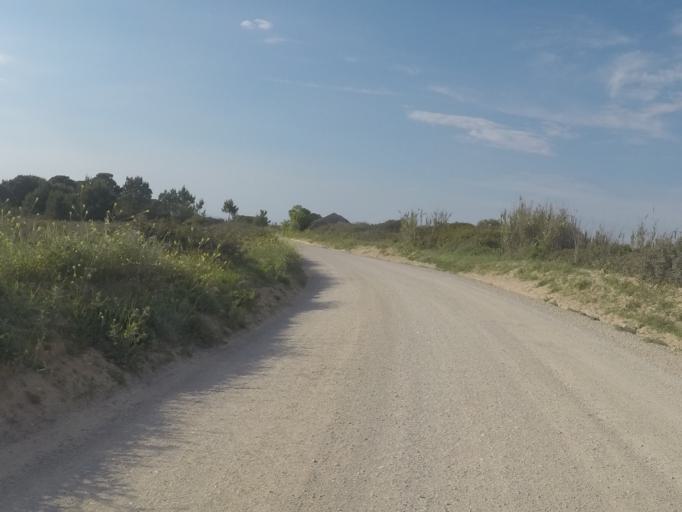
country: PT
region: Setubal
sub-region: Sesimbra
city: Sesimbra
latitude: 38.4445
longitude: -9.1971
